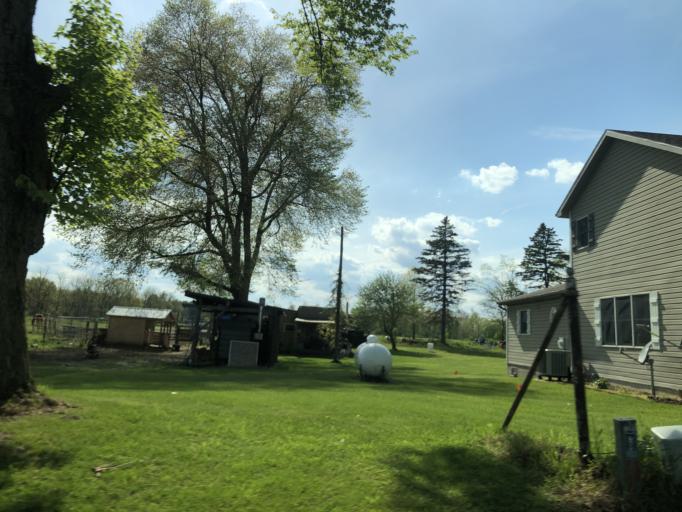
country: US
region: Michigan
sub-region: Hillsdale County
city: Reading
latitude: 41.7544
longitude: -84.8098
